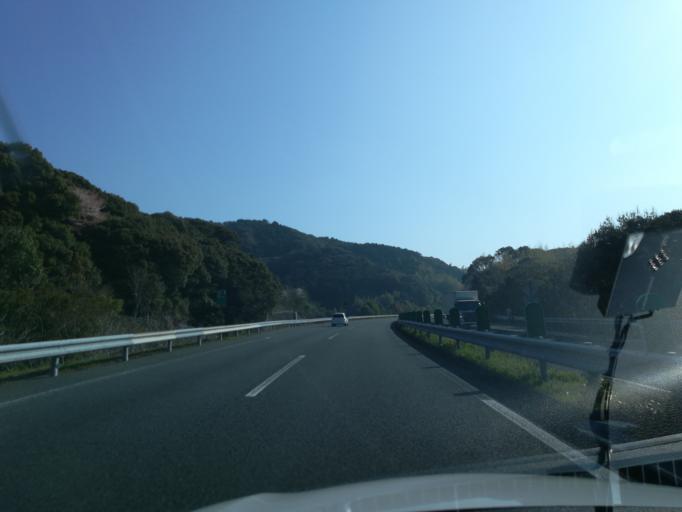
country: JP
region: Kochi
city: Kochi-shi
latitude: 33.6004
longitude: 133.6077
